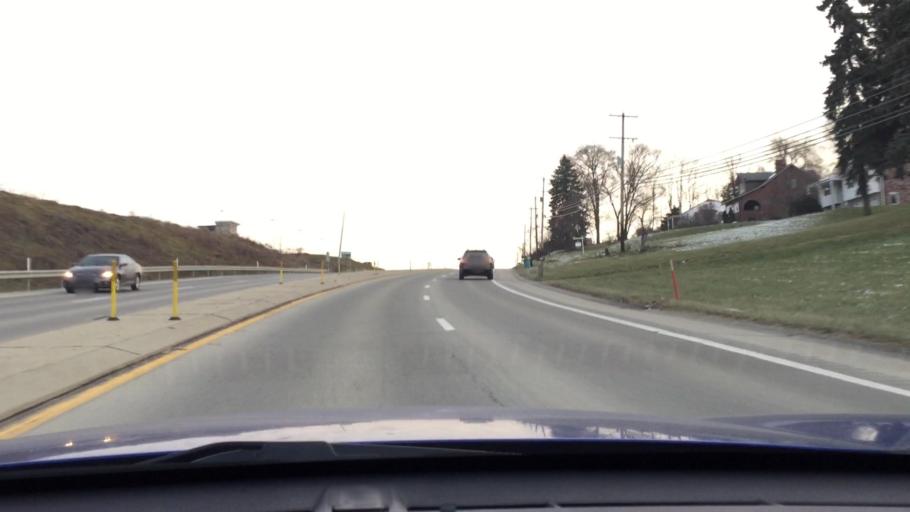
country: US
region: Pennsylvania
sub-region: Washington County
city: McGovern
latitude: 40.1985
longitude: -80.2086
